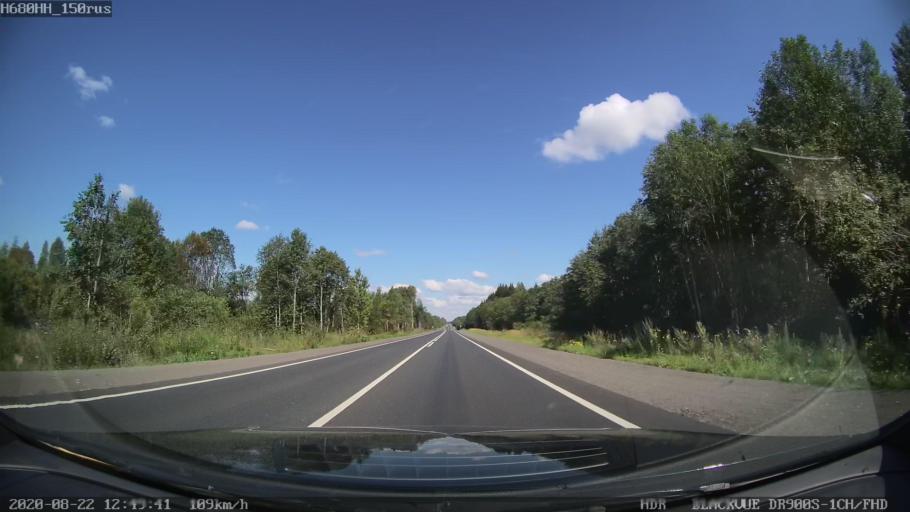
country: RU
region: Tverskaya
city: Rameshki
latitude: 57.4553
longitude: 36.2097
